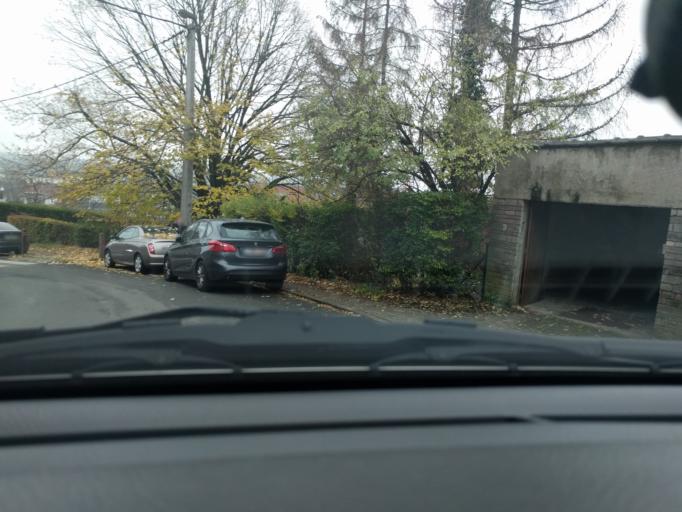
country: BE
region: Wallonia
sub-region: Province de Namur
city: Namur
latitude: 50.4694
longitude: 4.8754
